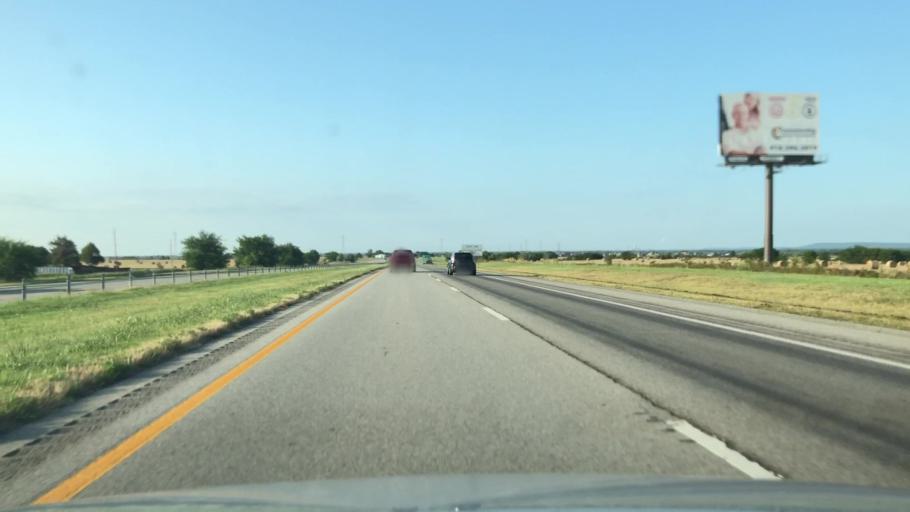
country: US
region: Oklahoma
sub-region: Osage County
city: Skiatook
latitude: 36.3603
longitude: -95.9208
